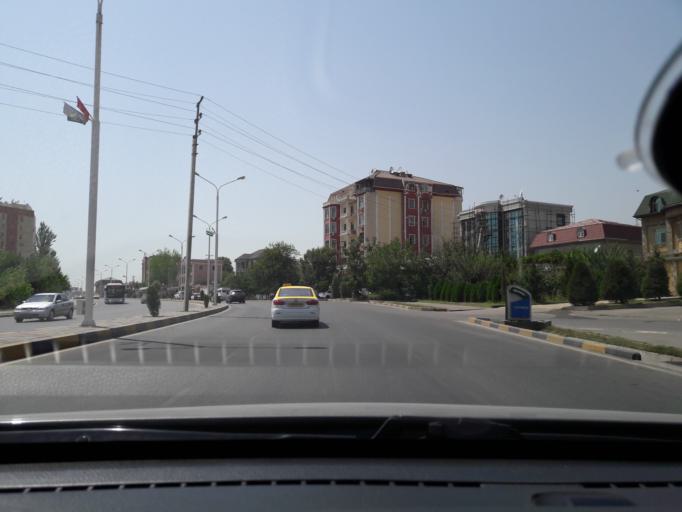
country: TJ
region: Dushanbe
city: Dushanbe
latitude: 38.5916
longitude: 68.7404
